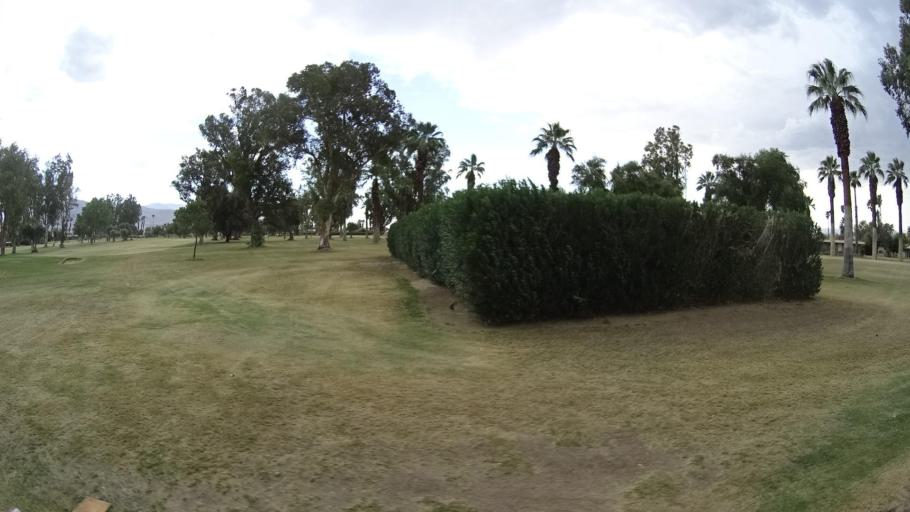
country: US
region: California
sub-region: San Diego County
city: Borrego Springs
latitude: 33.2860
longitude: -116.3892
